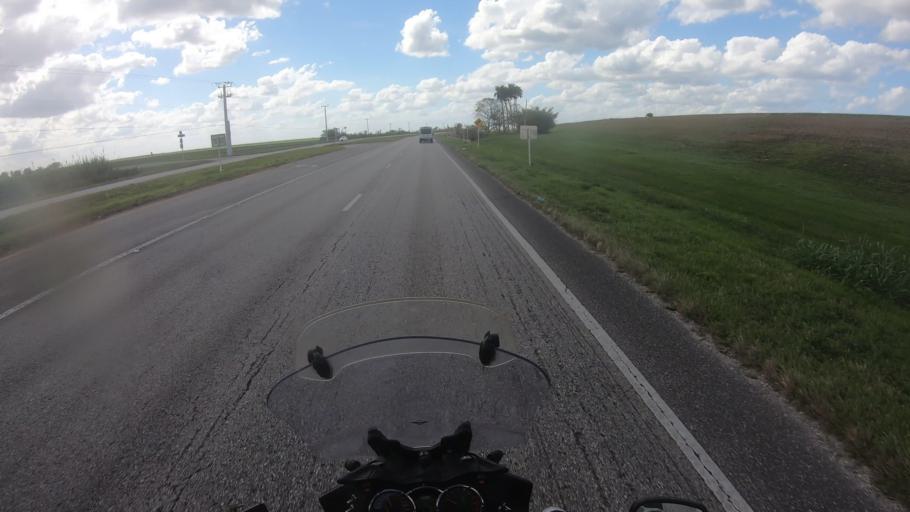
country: US
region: Florida
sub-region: Palm Beach County
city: South Bay
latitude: 26.6815
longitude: -80.7431
